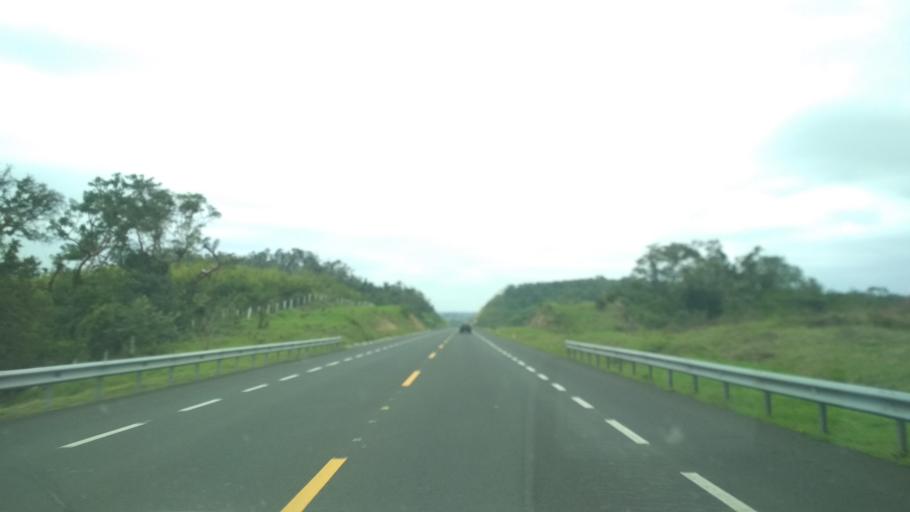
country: MX
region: Veracruz
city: Agua Dulce
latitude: 20.4193
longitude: -97.2141
